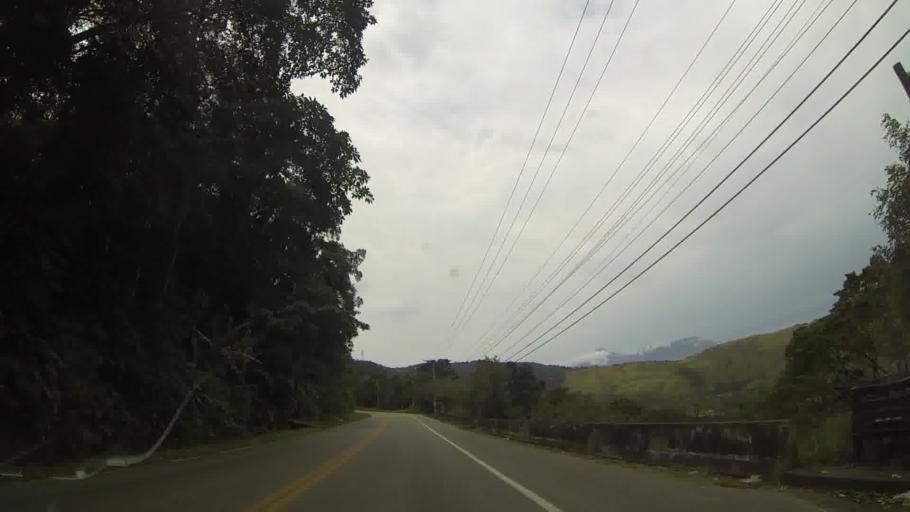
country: BR
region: Sao Paulo
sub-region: Sao Sebastiao
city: Sao Sebastiao
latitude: -23.8300
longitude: -45.5107
